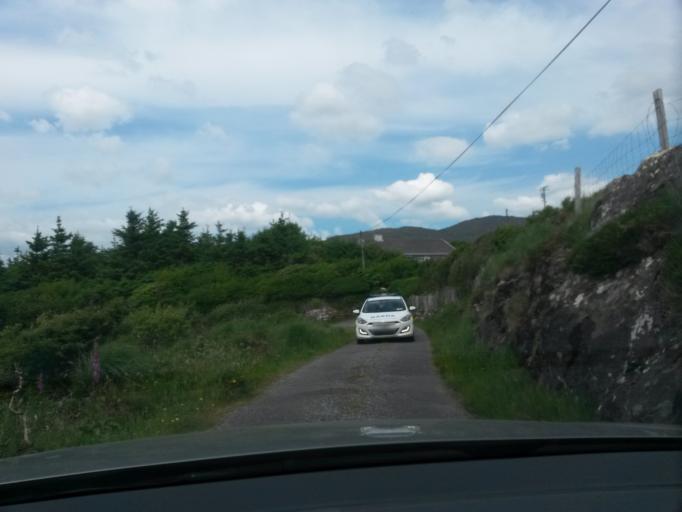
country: IE
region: Munster
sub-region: Ciarrai
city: Cahersiveen
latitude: 51.8013
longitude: -9.9470
